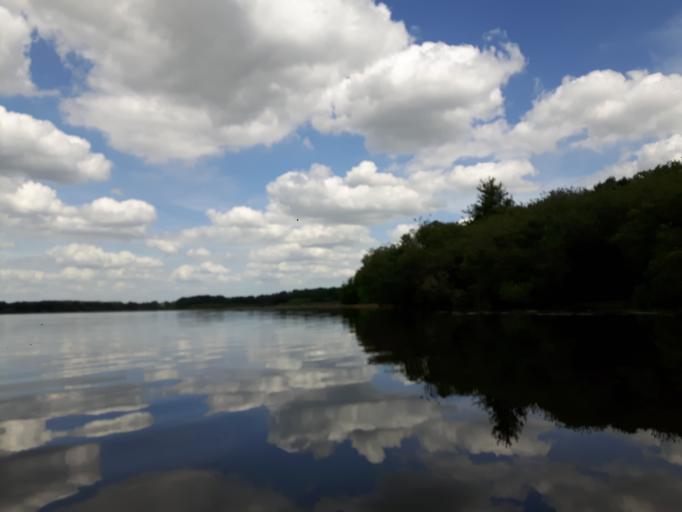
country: DE
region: Schleswig-Holstein
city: Muhbrook
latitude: 54.1407
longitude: 10.0075
